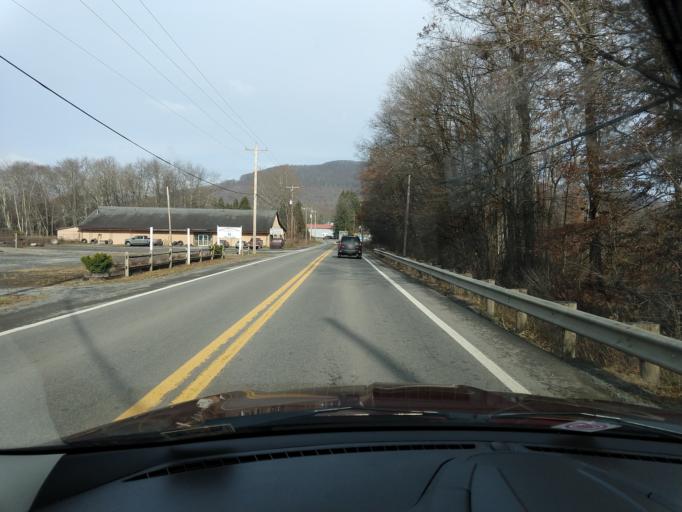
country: US
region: West Virginia
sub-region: Greenbrier County
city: Rainelle
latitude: 37.9588
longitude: -80.6837
